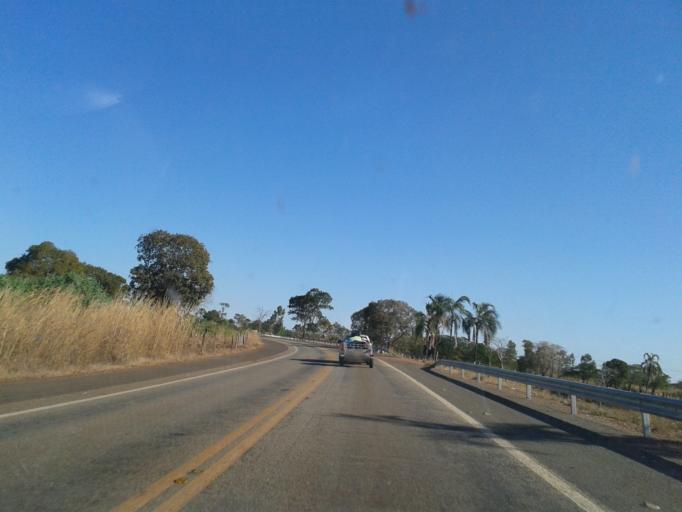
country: BR
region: Goias
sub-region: Mozarlandia
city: Mozarlandia
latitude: -15.0813
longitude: -50.6229
